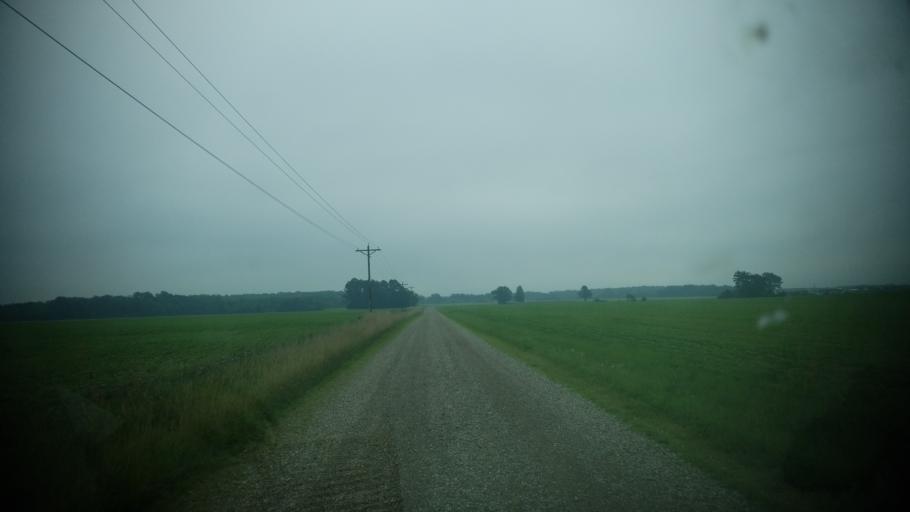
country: US
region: Illinois
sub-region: Clay County
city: Flora
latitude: 38.5881
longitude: -88.3720
